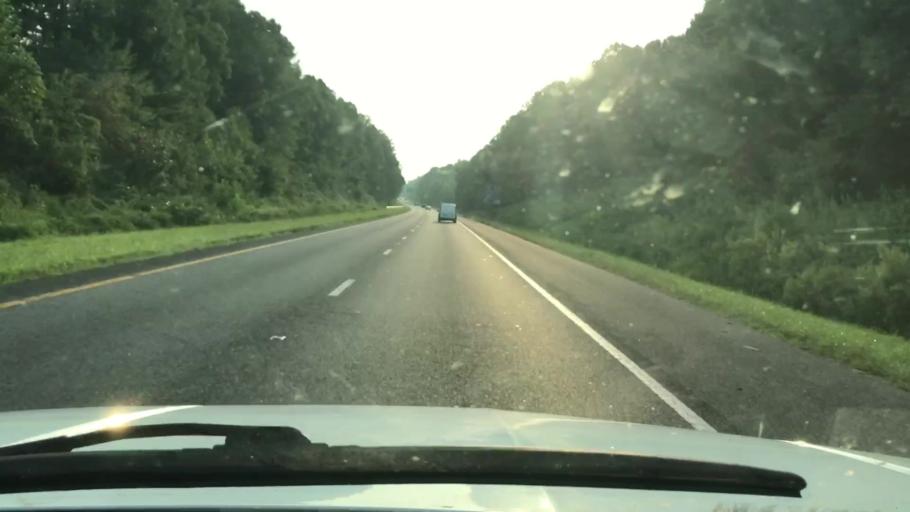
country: US
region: Virginia
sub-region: Chesterfield County
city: Brandermill
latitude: 37.4114
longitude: -77.5931
